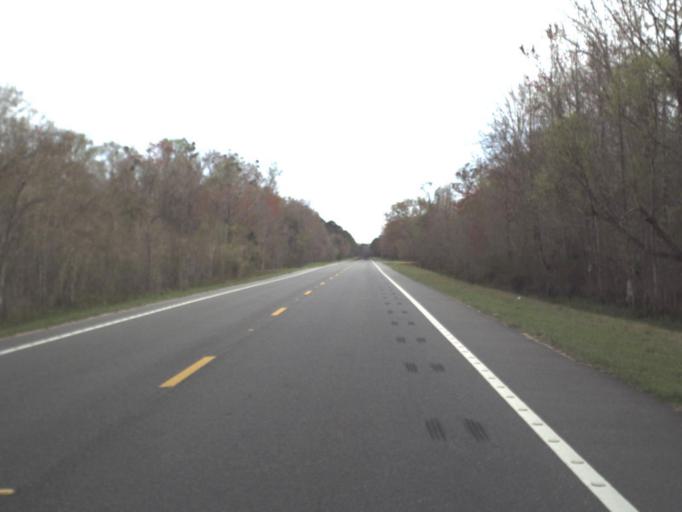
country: US
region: Florida
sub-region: Leon County
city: Woodville
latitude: 30.1760
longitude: -84.0098
